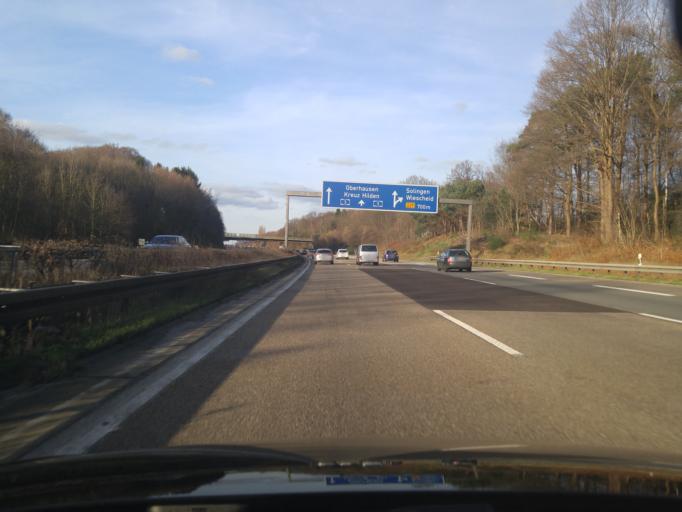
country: DE
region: North Rhine-Westphalia
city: Leichlingen
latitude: 51.1152
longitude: 6.9863
